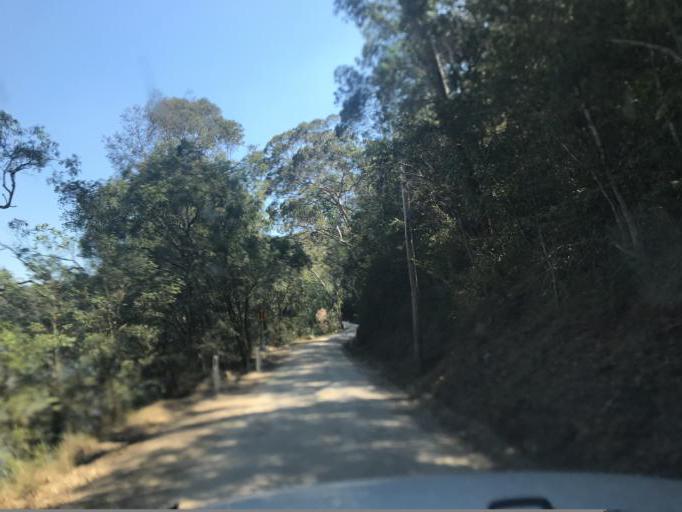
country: AU
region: New South Wales
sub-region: Hawkesbury
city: Pitt Town
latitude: -33.4184
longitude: 150.9059
